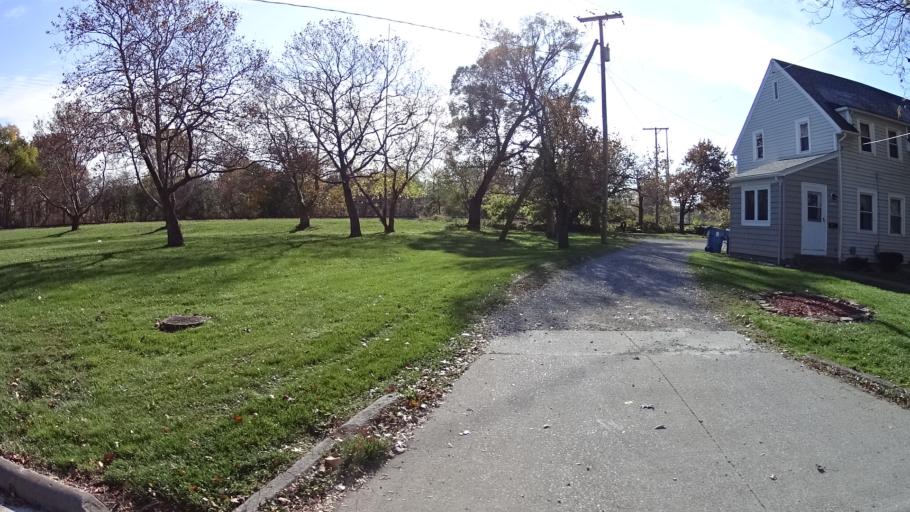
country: US
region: Ohio
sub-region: Lorain County
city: Lorain
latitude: 41.4715
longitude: -82.1558
